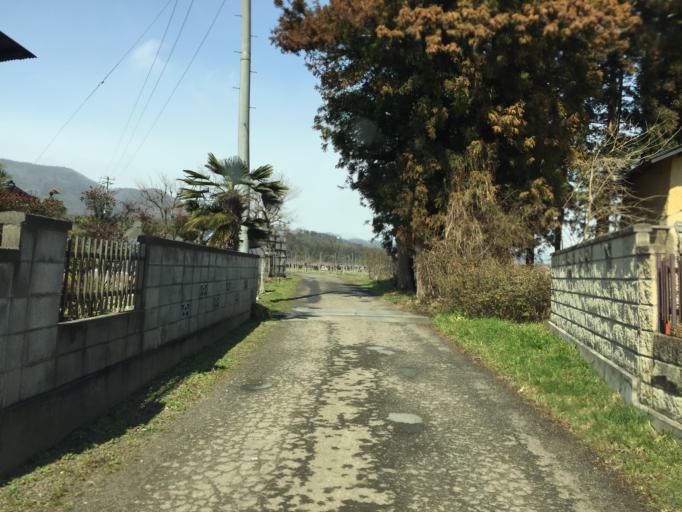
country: JP
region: Fukushima
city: Fukushima-shi
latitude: 37.7999
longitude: 140.4215
